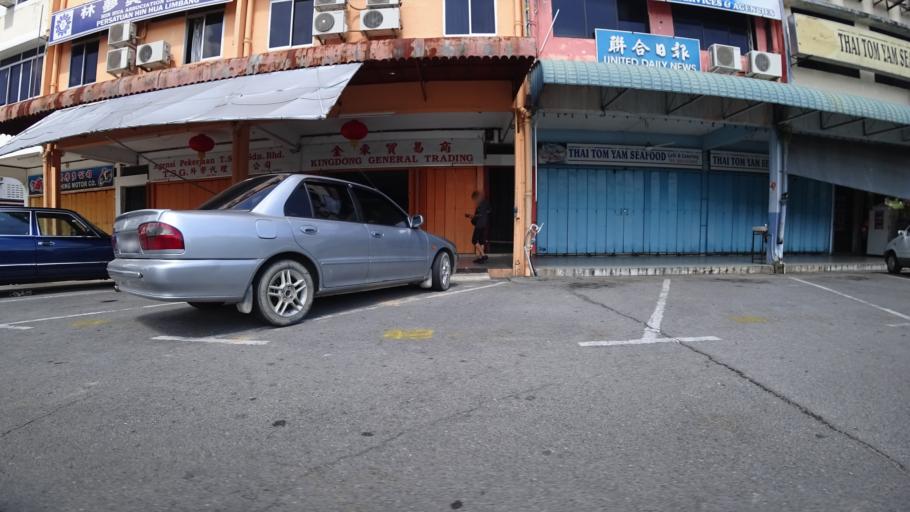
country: MY
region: Sarawak
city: Limbang
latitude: 4.7594
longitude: 115.0063
